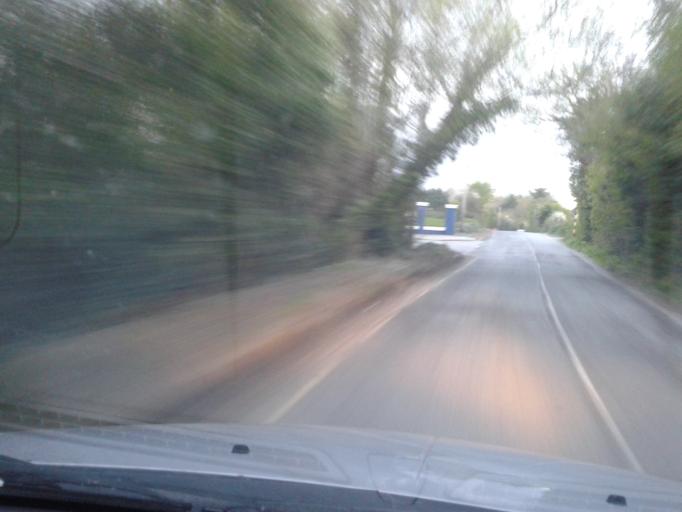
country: IE
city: Bonnybrook
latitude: 53.4199
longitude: -6.2139
